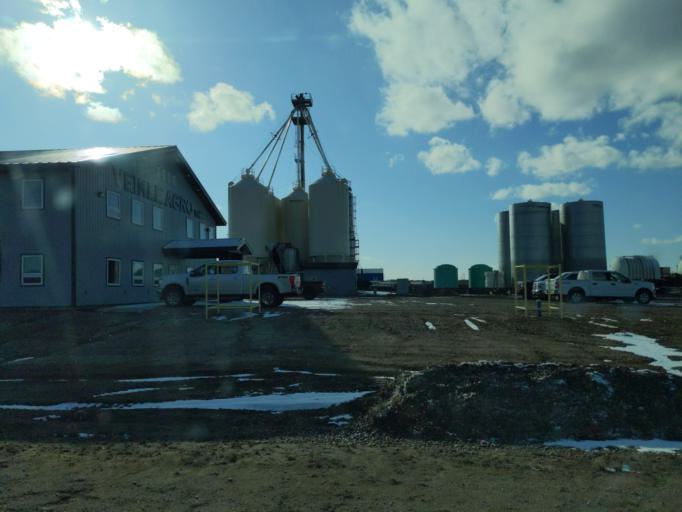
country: CA
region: Saskatchewan
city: Lloydminster
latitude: 53.2448
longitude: -109.9708
